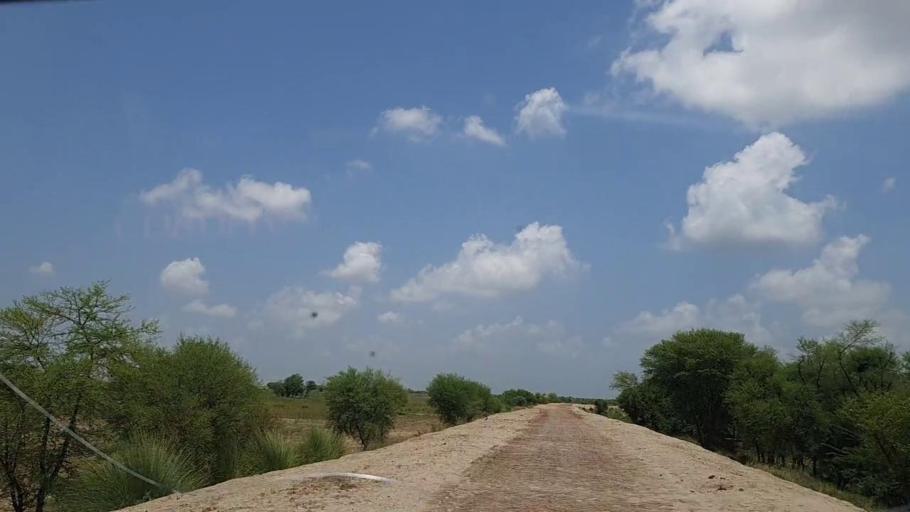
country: PK
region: Sindh
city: Tharu Shah
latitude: 26.9349
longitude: 67.9965
